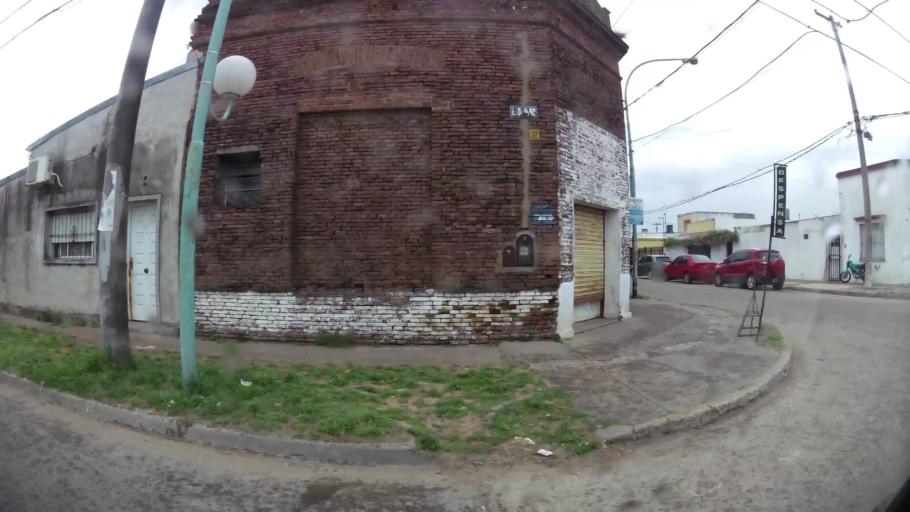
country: AR
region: Buenos Aires
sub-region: Partido de Zarate
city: Zarate
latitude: -34.0863
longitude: -59.0360
